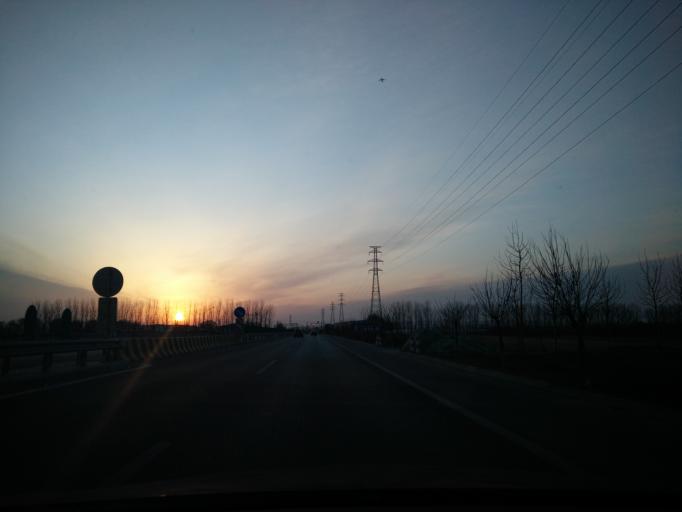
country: CN
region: Beijing
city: Qingyundian
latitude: 39.6929
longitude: 116.4801
